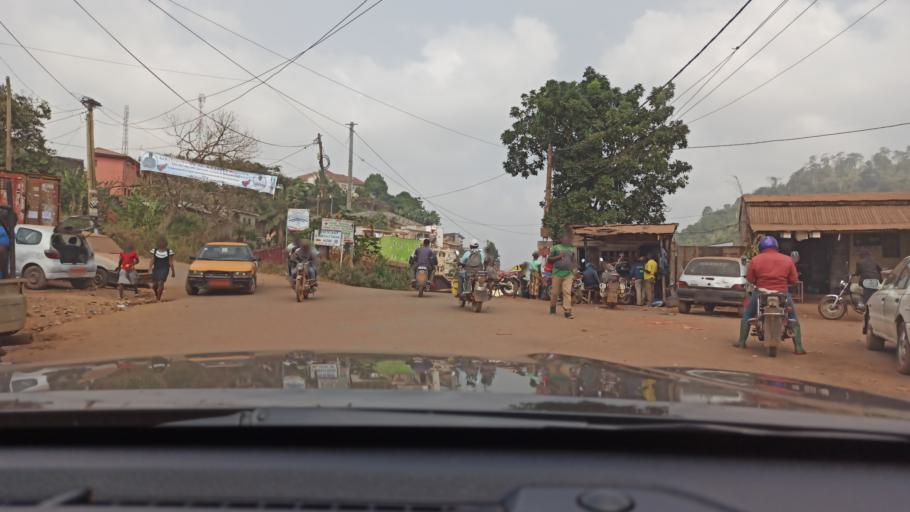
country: CM
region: Centre
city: Yaounde
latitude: 3.8773
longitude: 11.4813
